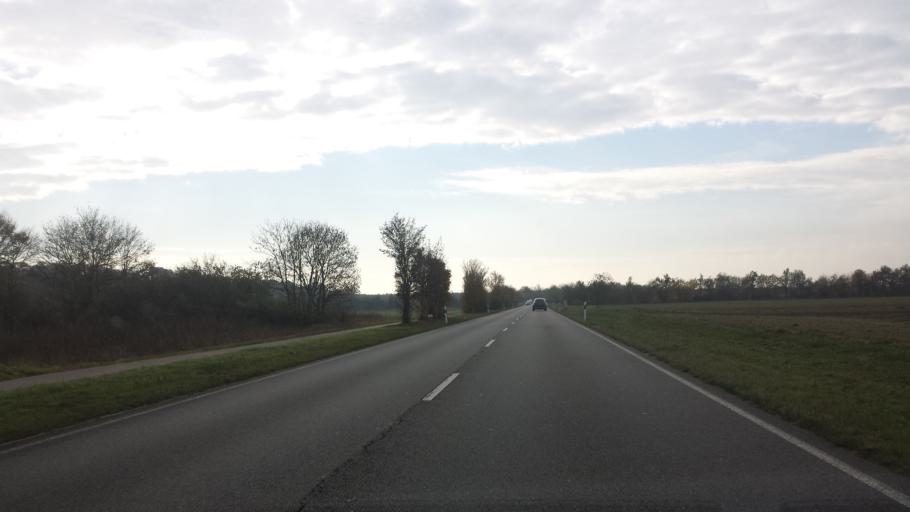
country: DE
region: Baden-Wuerttemberg
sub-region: Karlsruhe Region
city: Sankt Leon-Rot
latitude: 49.2847
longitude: 8.6268
